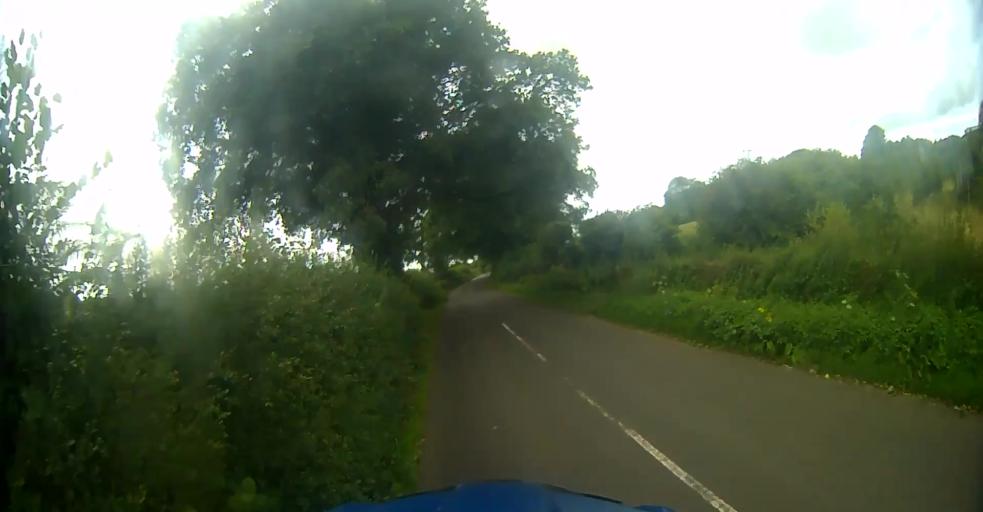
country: GB
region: England
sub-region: Hampshire
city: Alton
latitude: 51.1846
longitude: -1.0196
